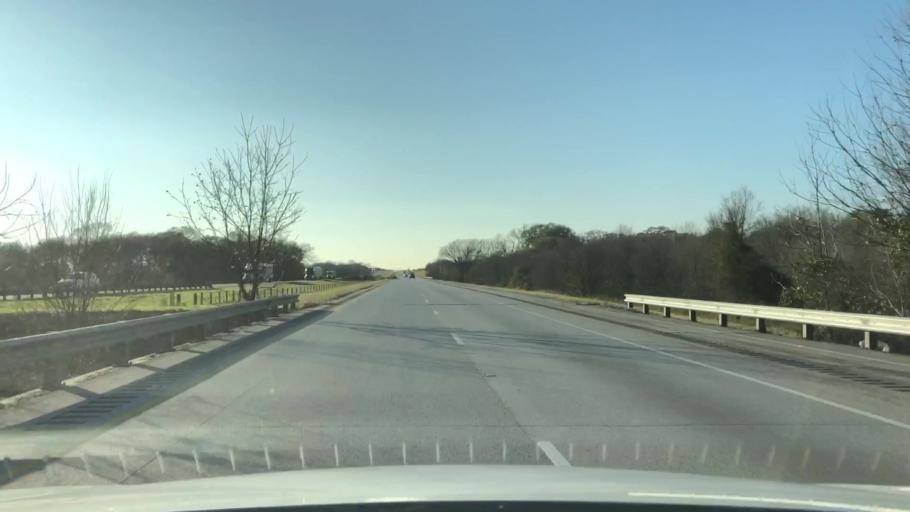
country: US
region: Texas
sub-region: Fayette County
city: Flatonia
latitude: 29.6922
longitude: -97.1854
